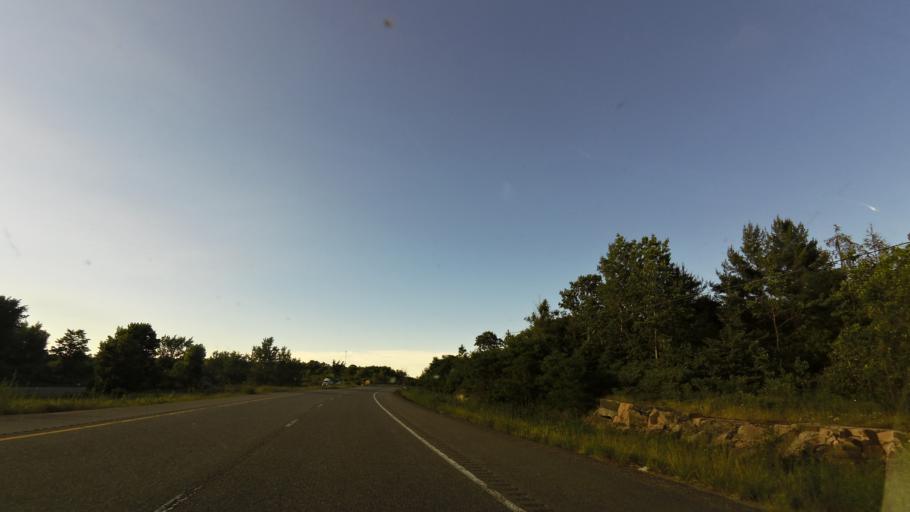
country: CA
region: Ontario
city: Midland
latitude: 44.8390
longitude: -79.7391
